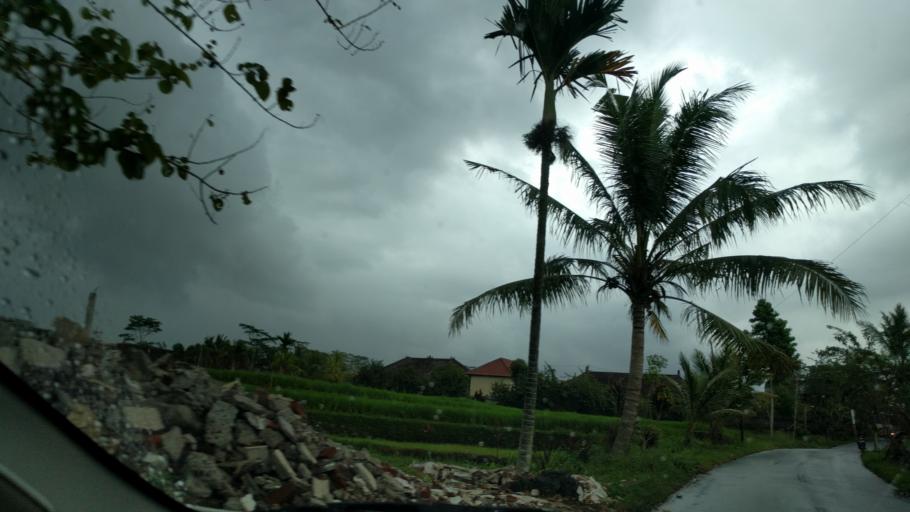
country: ID
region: Bali
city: Bunutan
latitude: -8.4650
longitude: 115.2597
